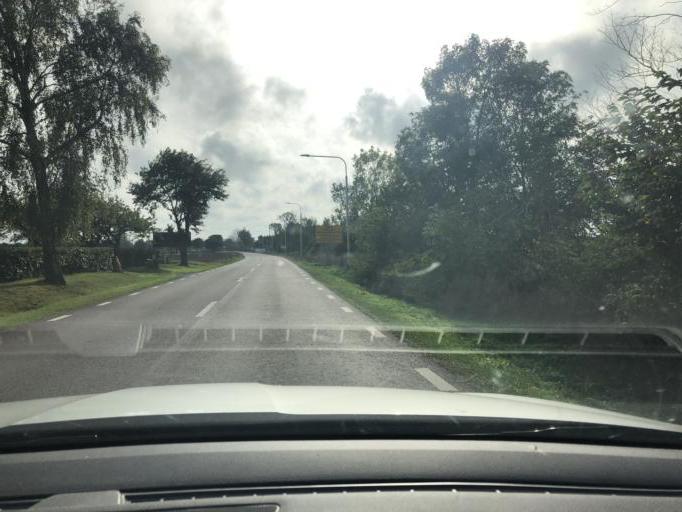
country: SE
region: Kalmar
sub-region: Morbylanga Kommun
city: Moerbylanga
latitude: 56.3634
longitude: 16.4227
